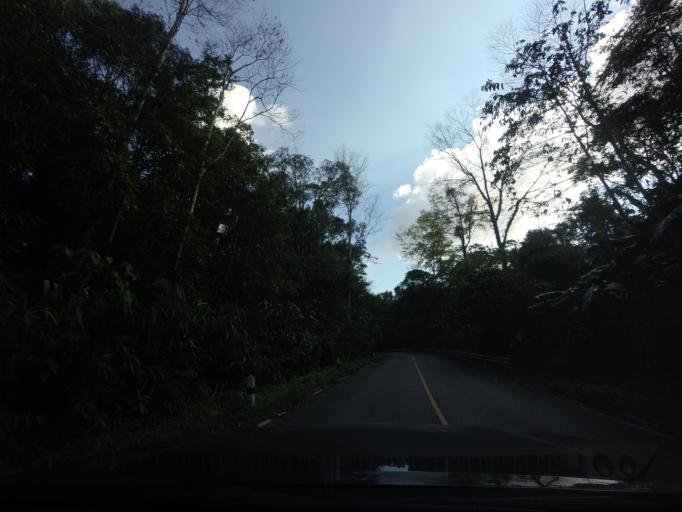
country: TH
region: Phetchabun
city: Lom Kao
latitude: 16.9285
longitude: 101.0716
